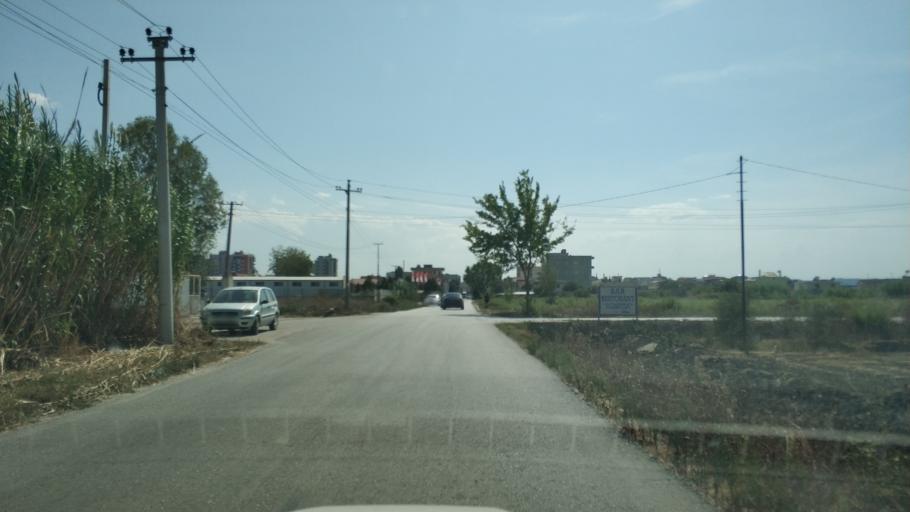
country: AL
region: Fier
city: Fier
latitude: 40.7408
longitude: 19.5595
